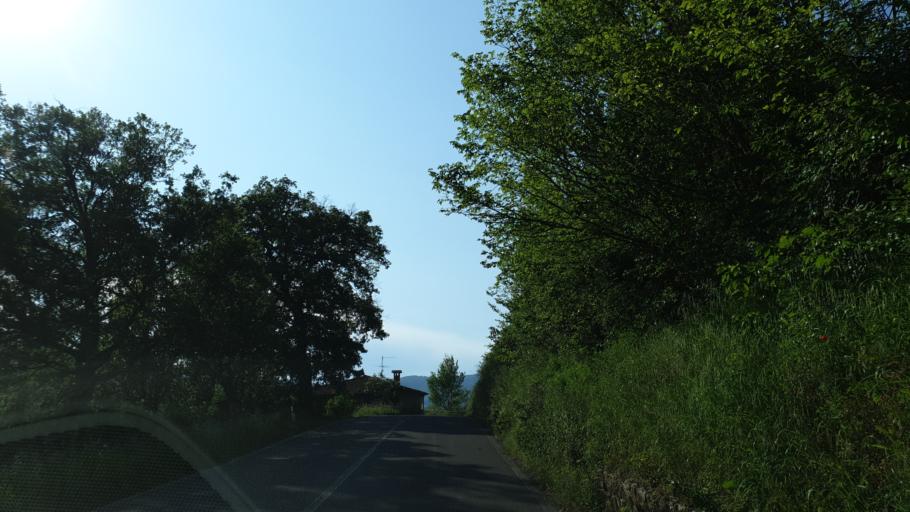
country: IT
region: Tuscany
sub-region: Province of Arezzo
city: Strada
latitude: 43.7467
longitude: 11.7273
